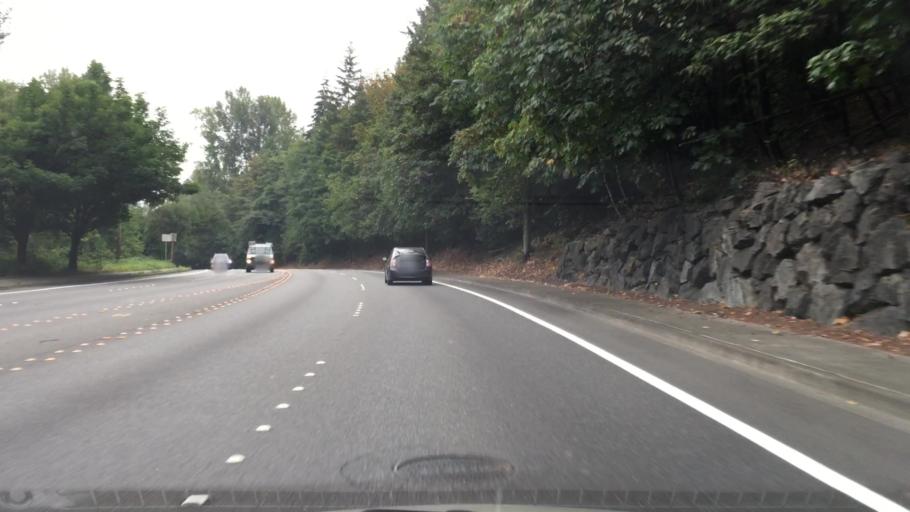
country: US
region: Washington
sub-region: King County
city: Newcastle
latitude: 47.5470
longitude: -122.1665
